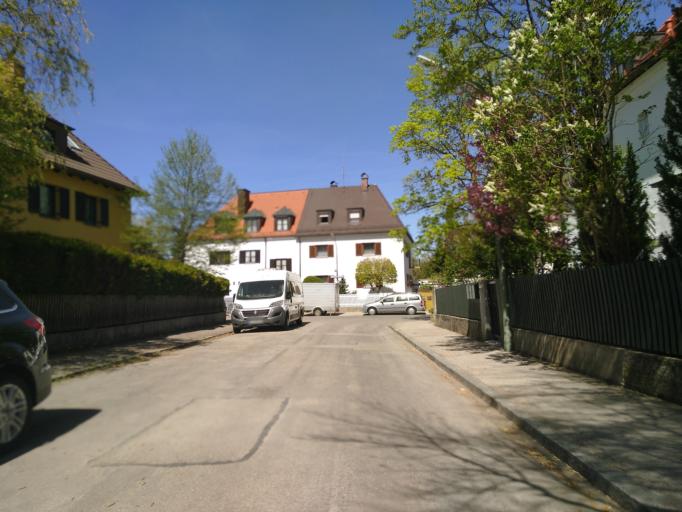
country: DE
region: Bavaria
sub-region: Upper Bavaria
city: Unterhaching
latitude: 48.0967
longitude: 11.6073
